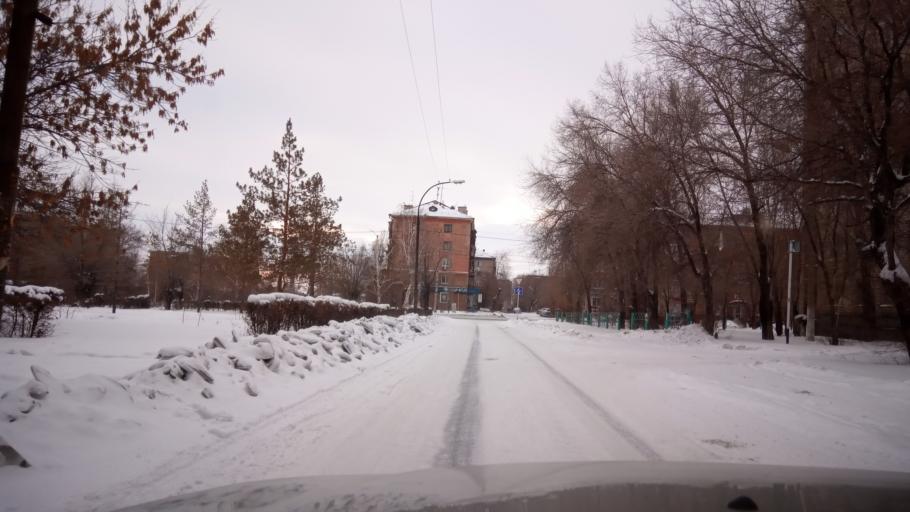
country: RU
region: Orenburg
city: Novotroitsk
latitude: 51.1971
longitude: 58.3067
